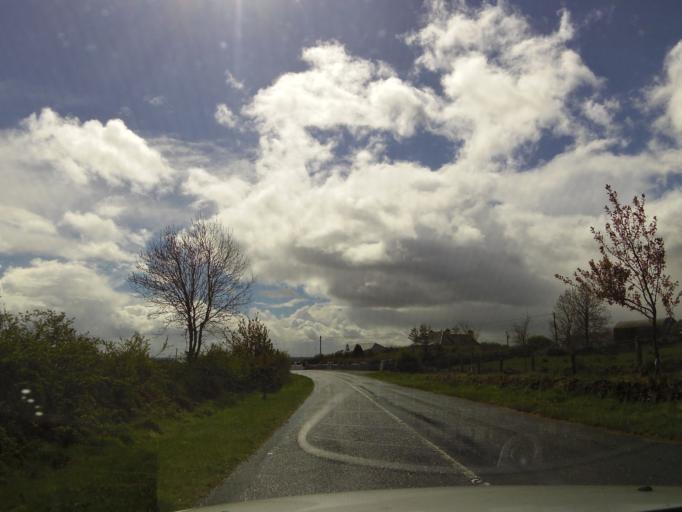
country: IE
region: Connaught
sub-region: Maigh Eo
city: Claremorris
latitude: 53.7626
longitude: -8.9645
